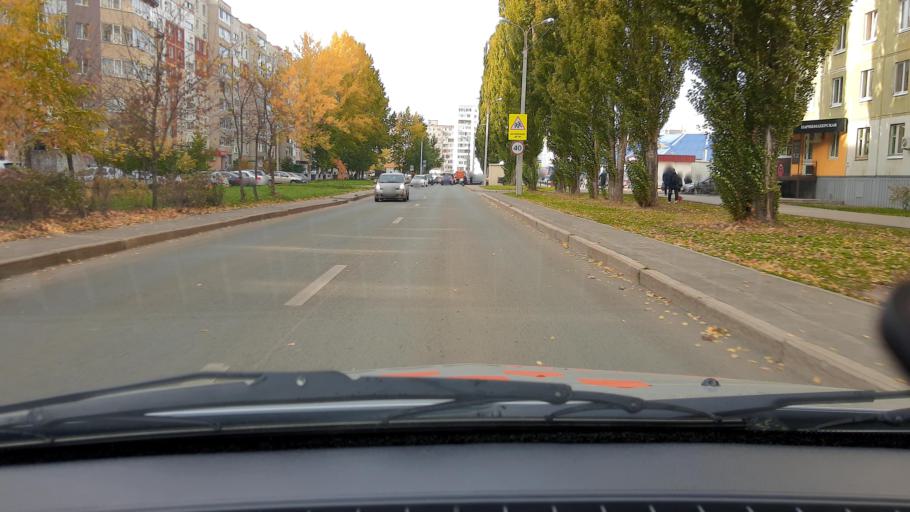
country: RU
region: Bashkortostan
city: Ufa
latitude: 54.7628
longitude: 56.0665
